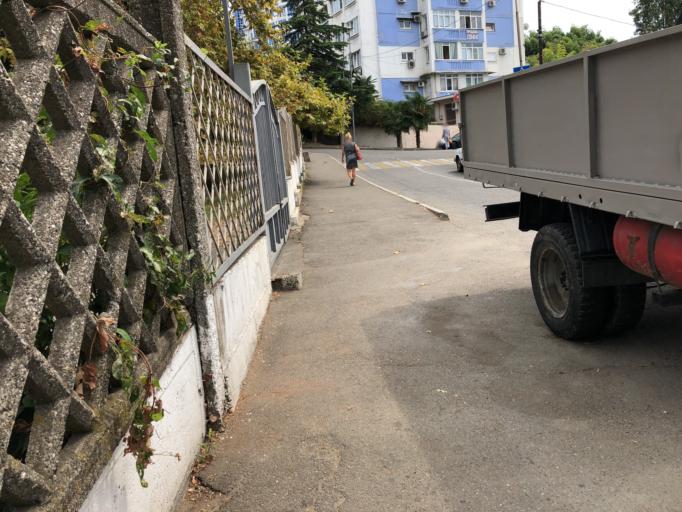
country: RU
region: Krasnodarskiy
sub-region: Sochi City
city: Sochi
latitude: 43.5911
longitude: 39.7369
